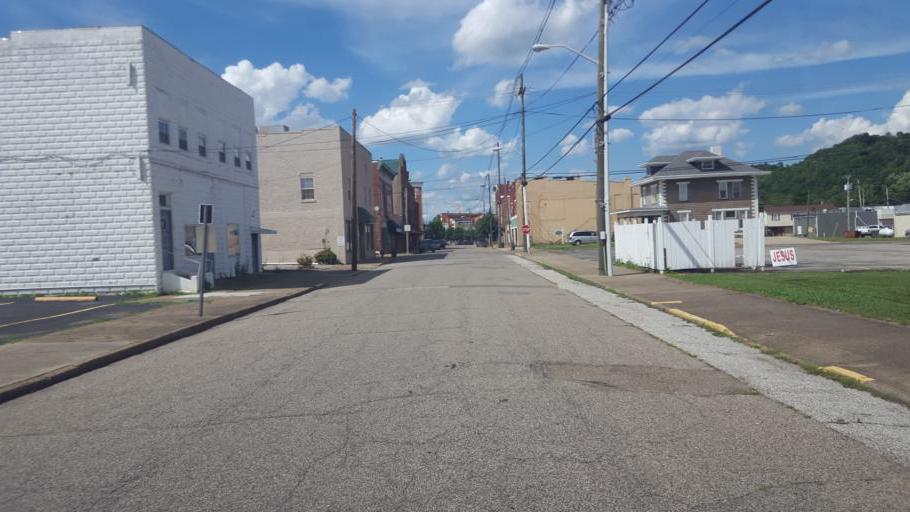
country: US
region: West Virginia
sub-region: Mason County
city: Point Pleasant
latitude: 38.8411
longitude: -82.1394
